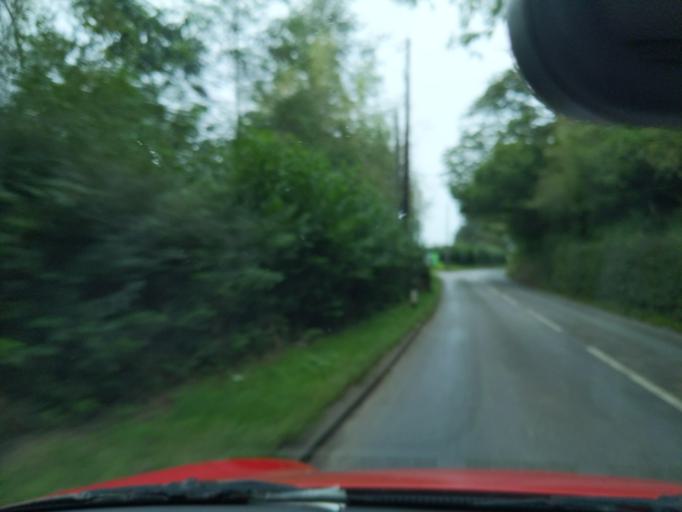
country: GB
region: England
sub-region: Devon
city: Okehampton
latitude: 50.8318
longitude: -4.0743
